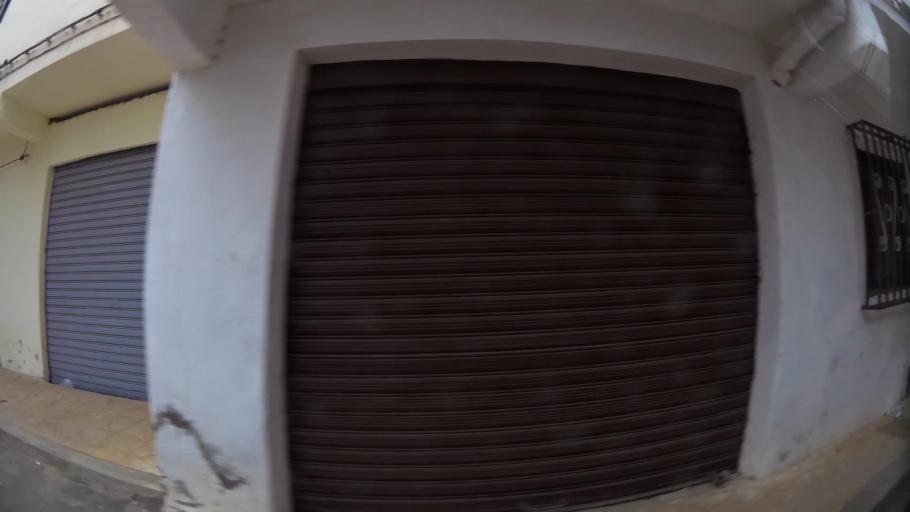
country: MA
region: Oriental
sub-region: Nador
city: Nador
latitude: 35.1577
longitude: -2.9129
